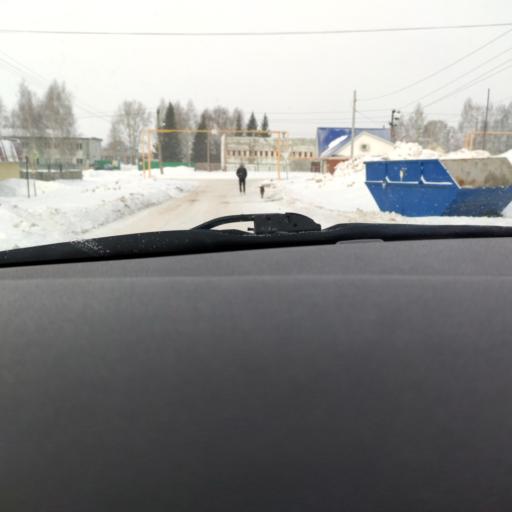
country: RU
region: Bashkortostan
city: Blagoveshchensk
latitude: 55.0282
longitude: 56.0028
